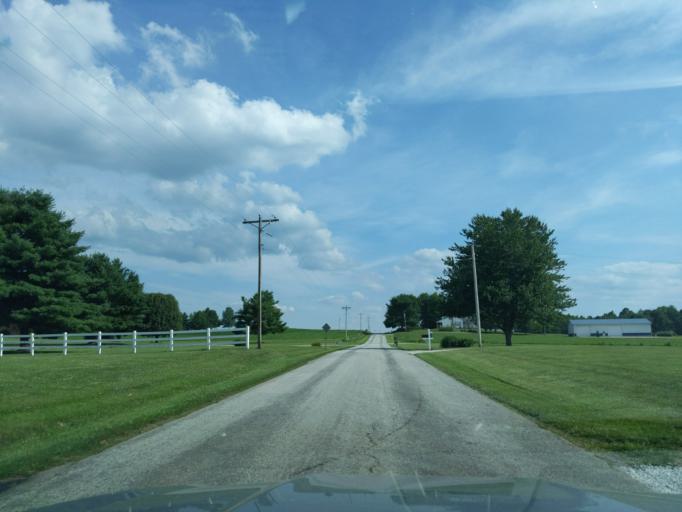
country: US
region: Indiana
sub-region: Decatur County
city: Greensburg
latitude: 39.2866
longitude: -85.4666
